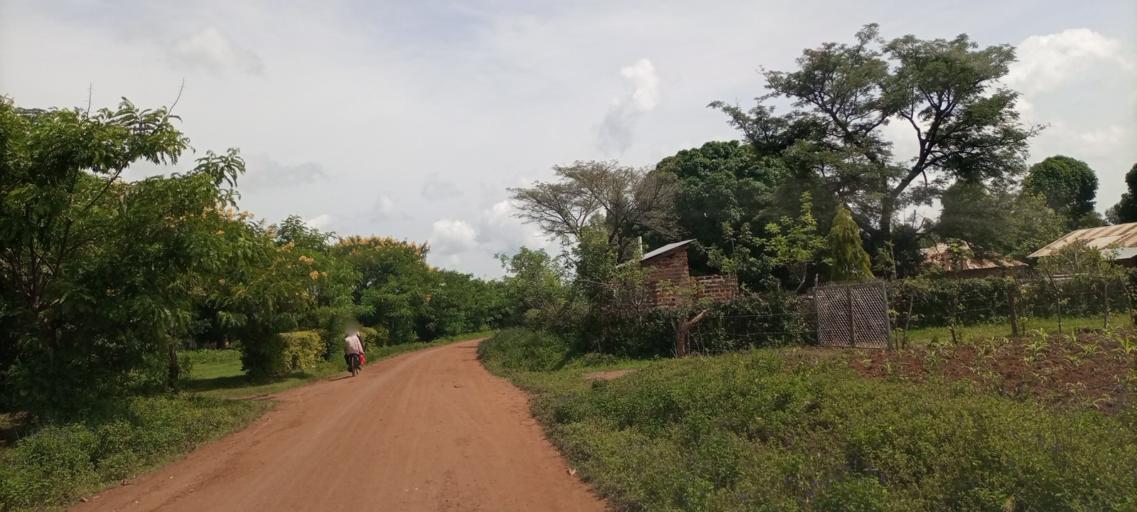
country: UG
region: Eastern Region
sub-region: Budaka District
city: Budaka
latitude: 1.1755
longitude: 33.9248
